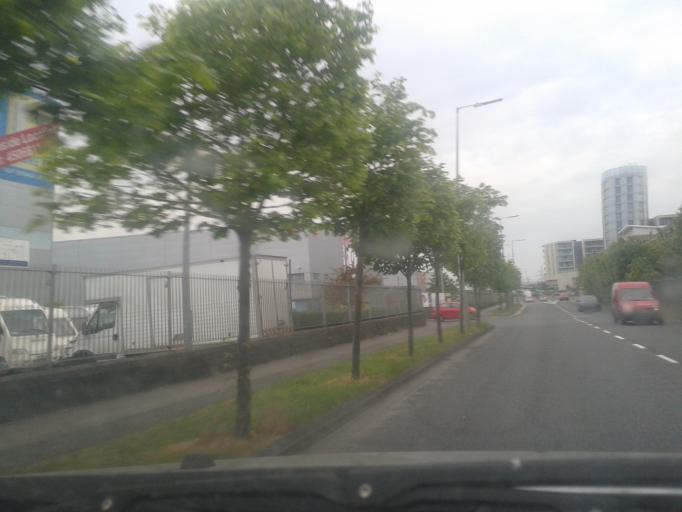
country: IE
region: Leinster
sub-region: Dublin City
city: Finglas
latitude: 53.4022
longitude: -6.2994
